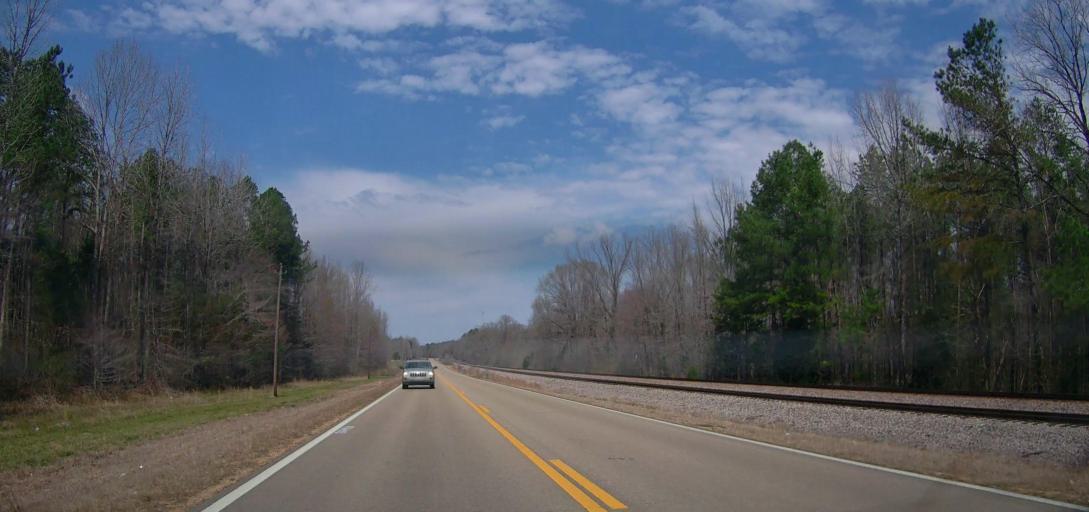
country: US
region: Mississippi
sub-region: Union County
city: New Albany
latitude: 34.5882
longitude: -89.1340
